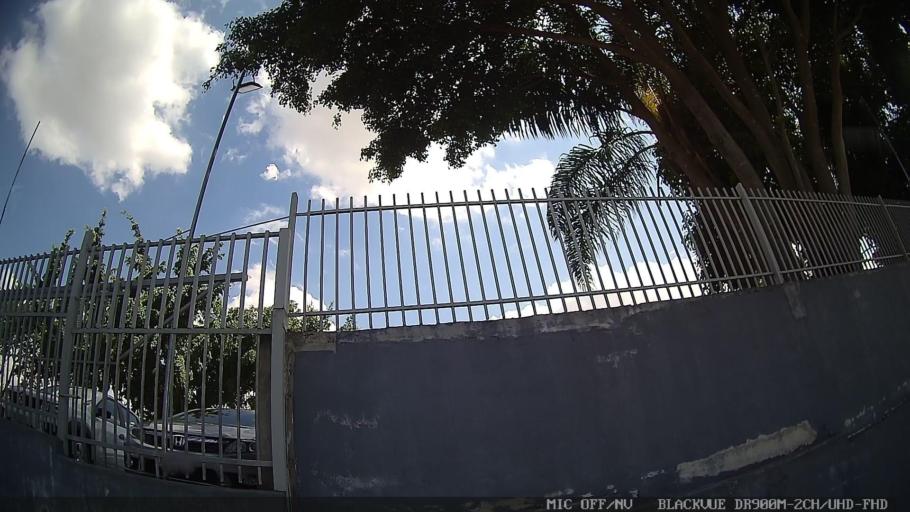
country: BR
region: Sao Paulo
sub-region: Guarulhos
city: Guarulhos
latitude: -23.4944
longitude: -46.4707
